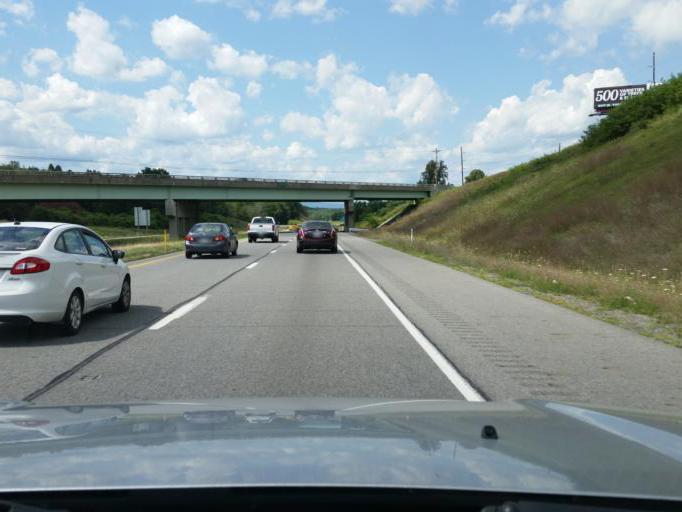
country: US
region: Pennsylvania
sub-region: Bedford County
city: Bedford
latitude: 40.0857
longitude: -78.5289
